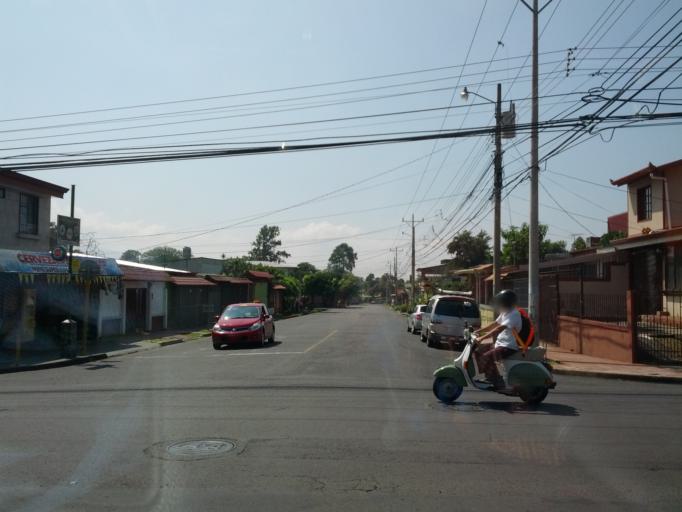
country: CR
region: Alajuela
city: Alajuela
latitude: 10.0143
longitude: -84.2025
